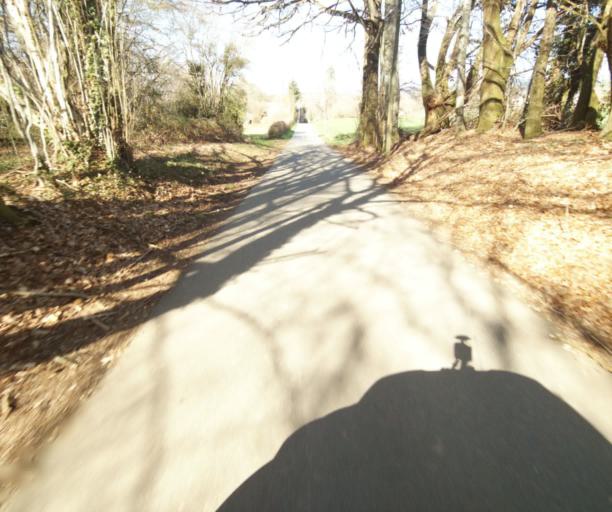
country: FR
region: Limousin
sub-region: Departement de la Correze
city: Chamboulive
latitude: 45.4799
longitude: 1.7398
